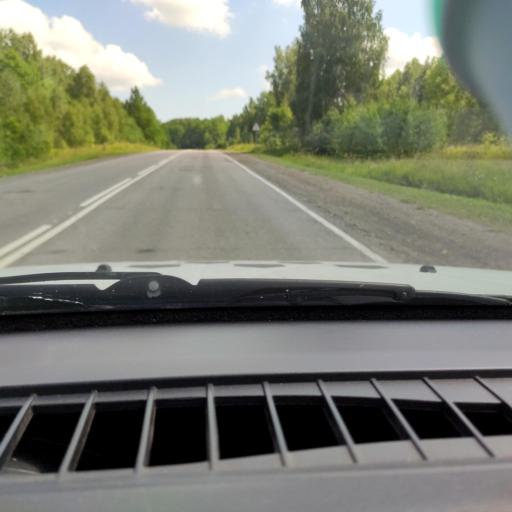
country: RU
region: Bashkortostan
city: Verkhniye Kigi
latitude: 55.3874
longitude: 58.6645
